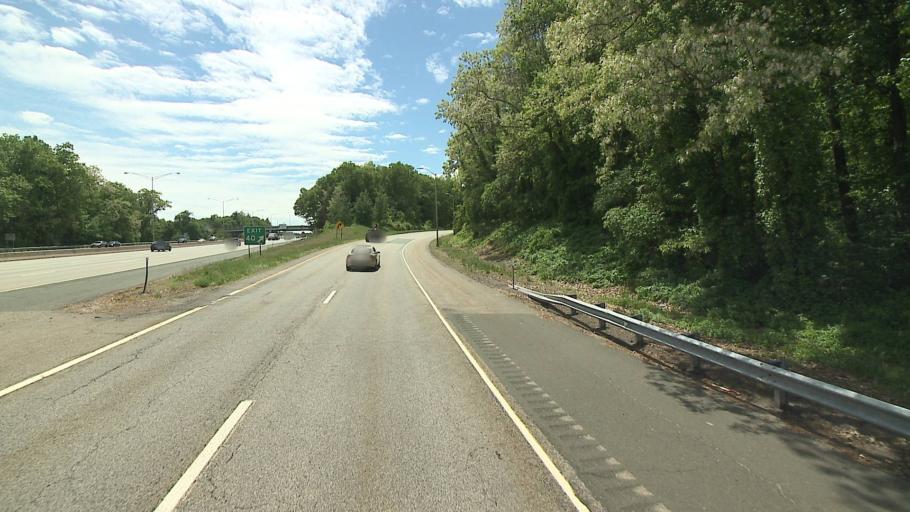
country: US
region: Connecticut
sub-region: Hartford County
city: Windsor Locks
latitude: 41.9018
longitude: -72.6373
